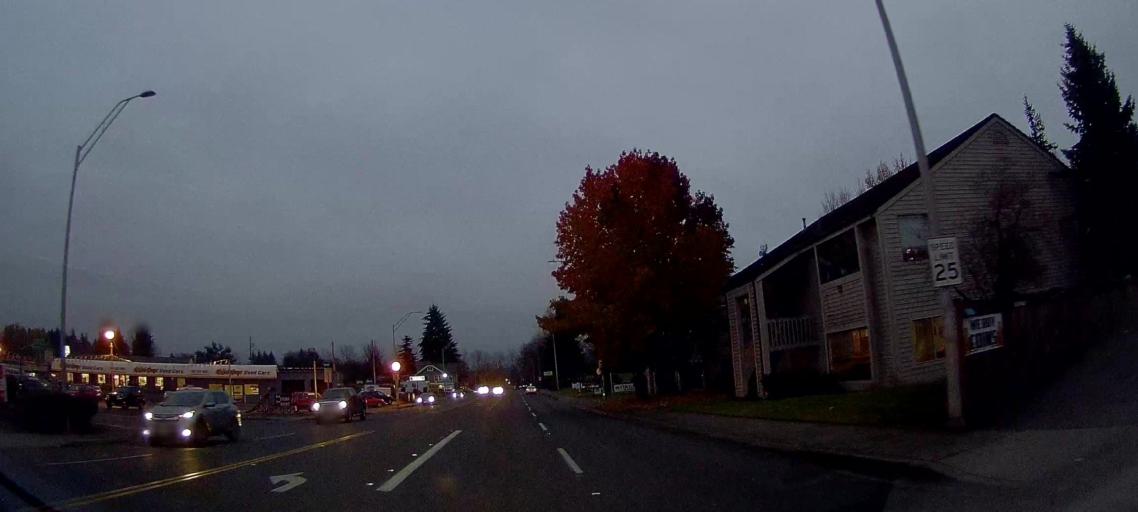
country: US
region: Washington
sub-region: Thurston County
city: Olympia
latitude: 47.0455
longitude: -122.8684
